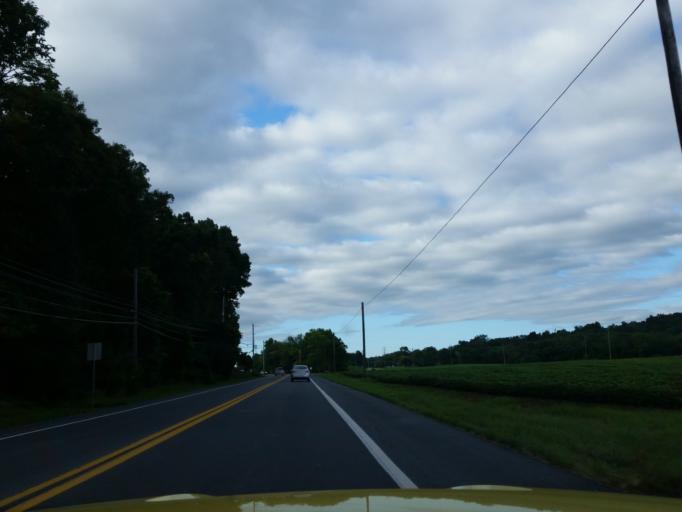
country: US
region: Pennsylvania
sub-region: Dauphin County
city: Hershey
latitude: 40.2431
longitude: -76.6256
